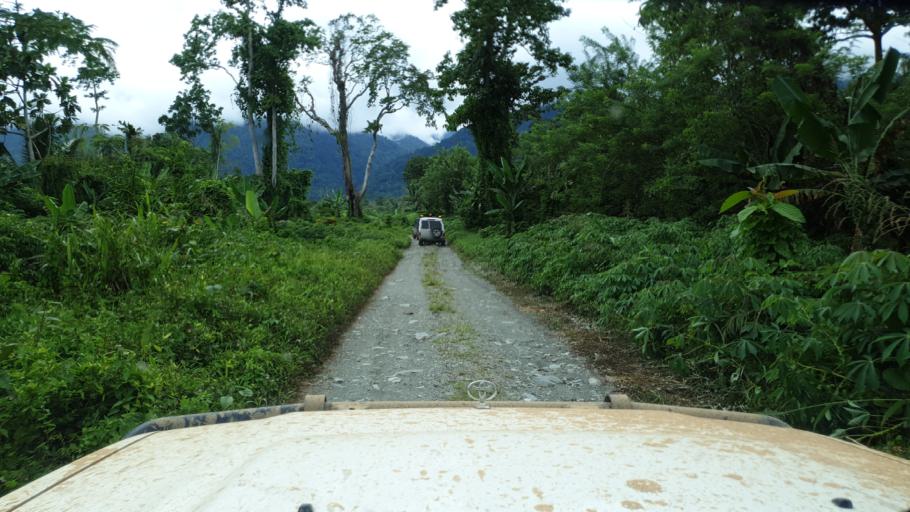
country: PG
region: Northern Province
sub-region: Sohe
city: Kokoda
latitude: -8.9373
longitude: 147.8676
